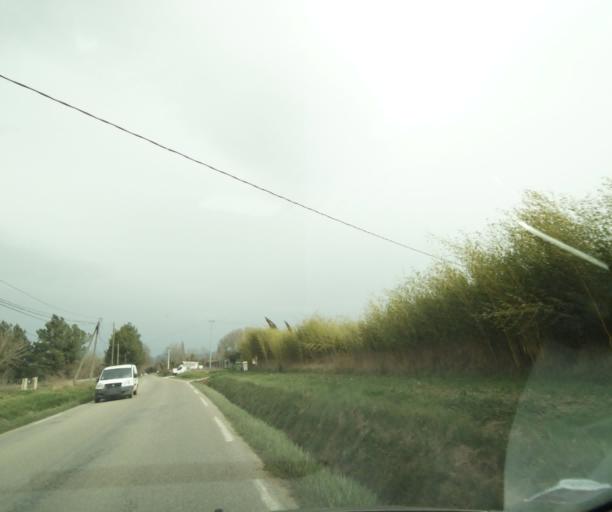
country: FR
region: Provence-Alpes-Cote d'Azur
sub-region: Departement des Bouches-du-Rhone
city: Trets
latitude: 43.4587
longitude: 5.6982
